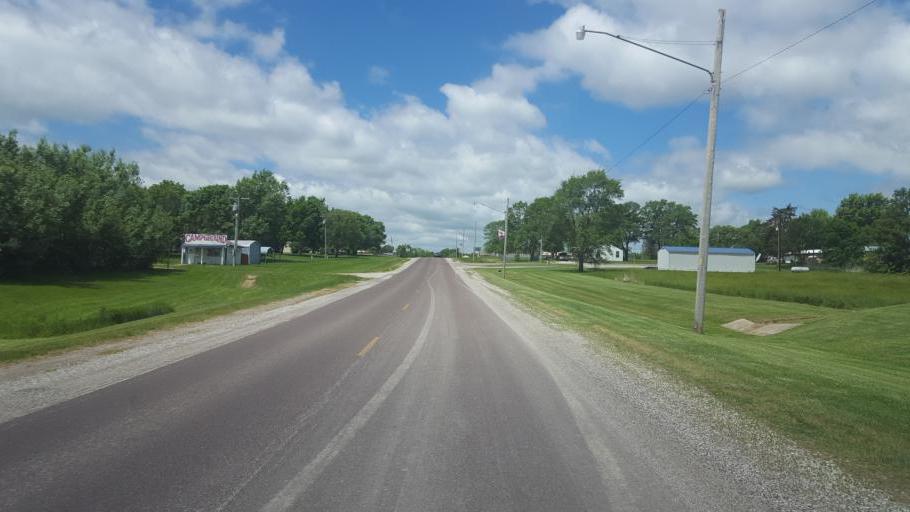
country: US
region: Iowa
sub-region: Decatur County
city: Lamoni
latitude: 40.4675
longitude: -93.9839
